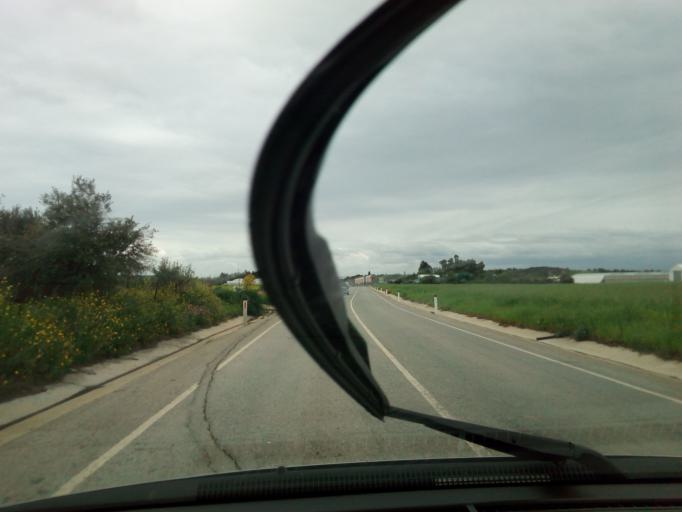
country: CY
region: Larnaka
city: Kofinou
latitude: 34.7487
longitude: 33.3179
